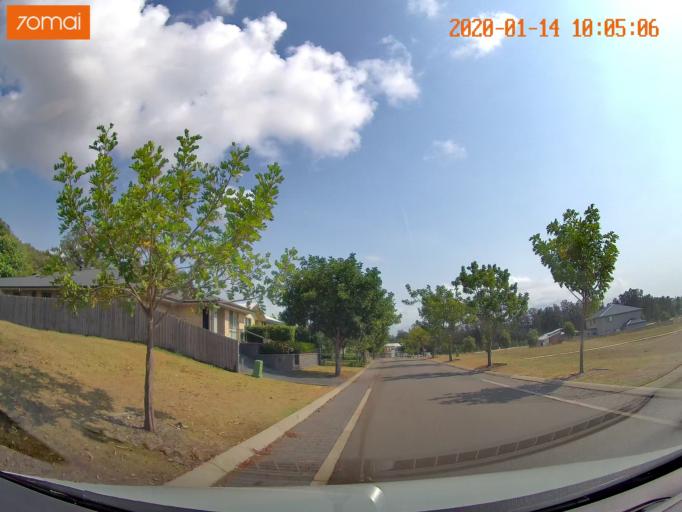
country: AU
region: New South Wales
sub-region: Wyong Shire
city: Kingfisher Shores
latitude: -33.1253
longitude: 151.5372
